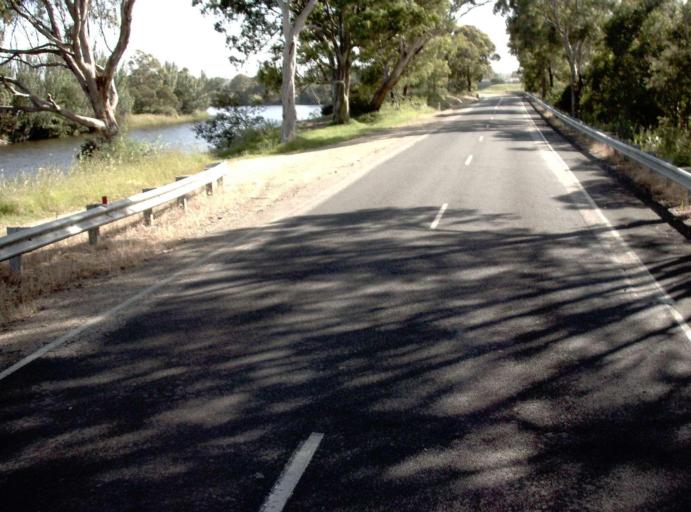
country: AU
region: Victoria
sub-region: East Gippsland
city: Lakes Entrance
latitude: -37.8420
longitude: 147.8571
